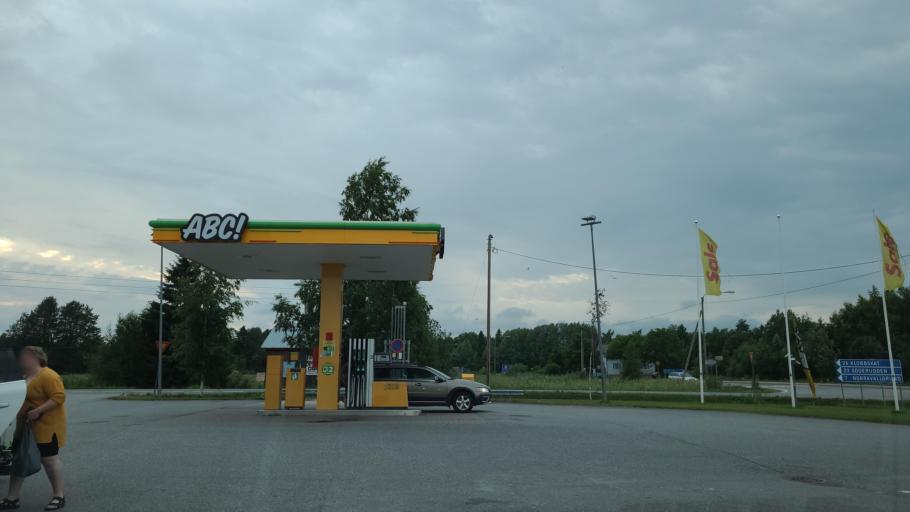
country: FI
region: Ostrobothnia
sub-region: Vaasa
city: Replot
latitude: 63.2318
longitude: 21.4077
